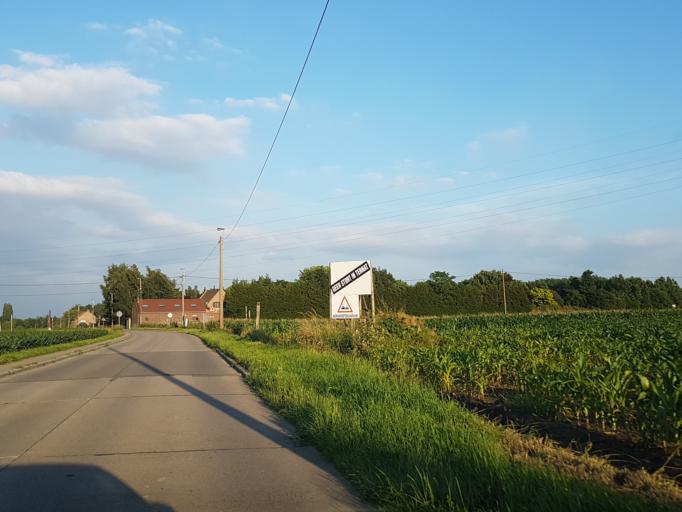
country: BE
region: Flanders
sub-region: Provincie Vlaams-Brabant
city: Ternat
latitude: 50.8650
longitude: 4.1876
